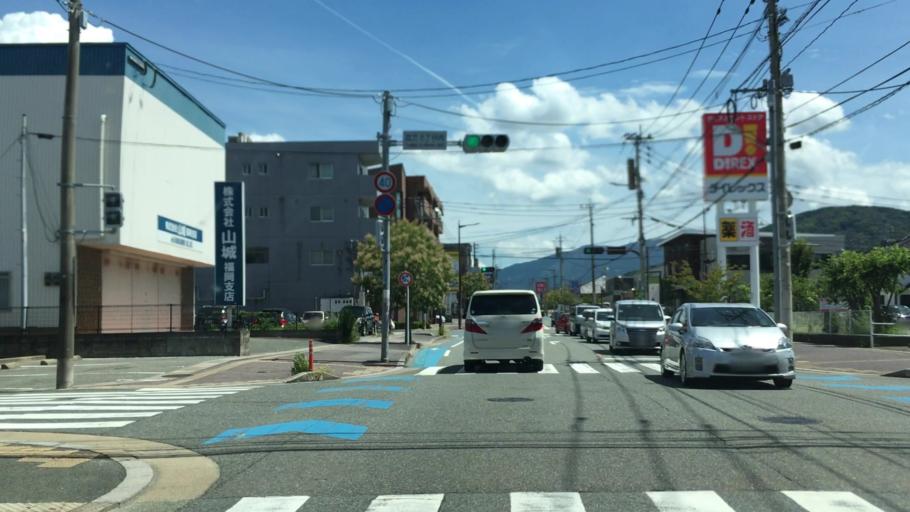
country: JP
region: Fukuoka
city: Onojo
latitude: 33.5434
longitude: 130.4785
